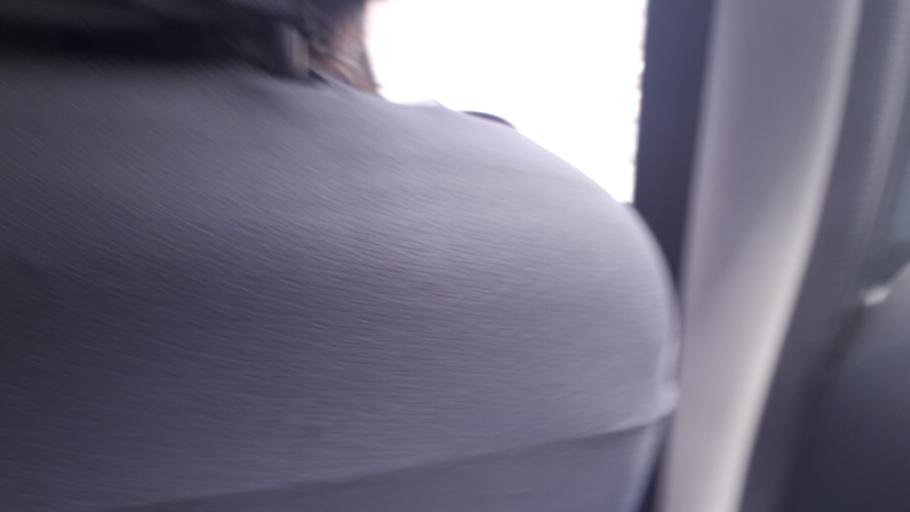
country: AR
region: Jujuy
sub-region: Departamento de Tumbaya
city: Tumbaya
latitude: -23.7464
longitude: -65.4789
